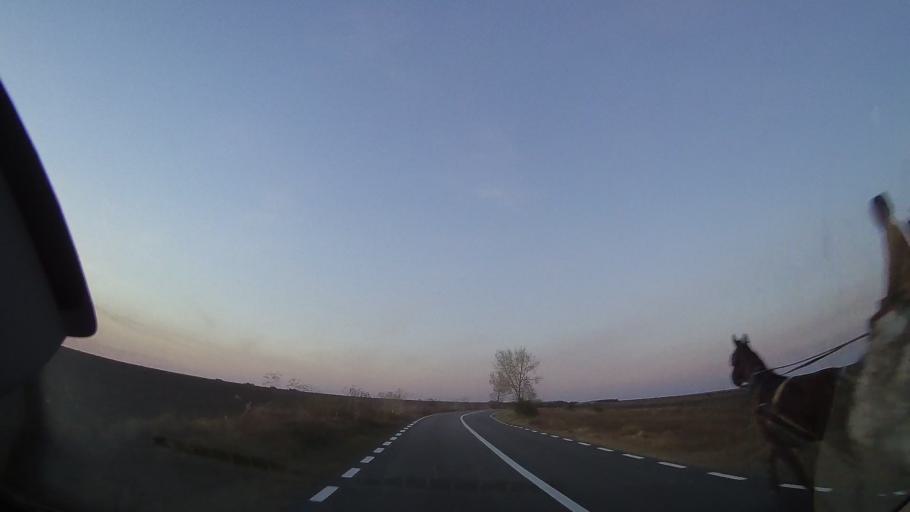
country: RO
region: Constanta
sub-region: Comuna Cobadin
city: Cobadin
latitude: 44.0270
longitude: 28.2632
